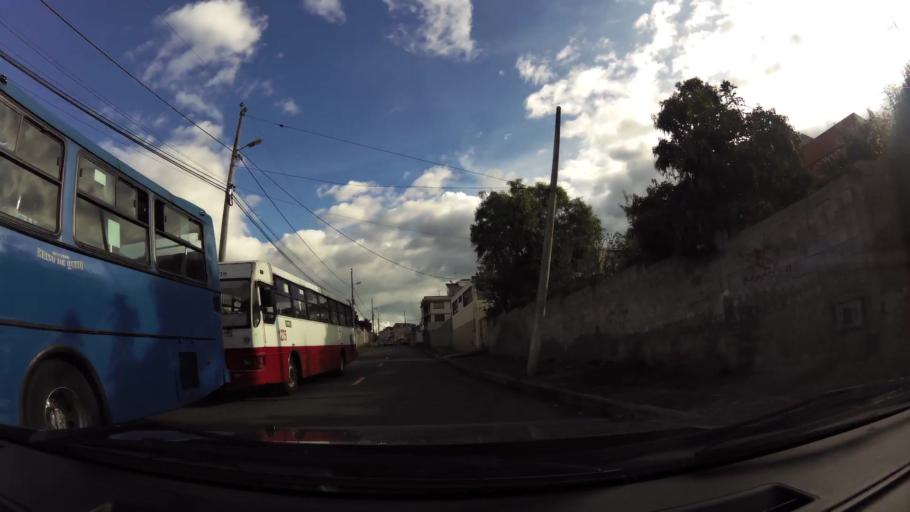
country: EC
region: Pichincha
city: Quito
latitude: -0.1341
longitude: -78.4560
